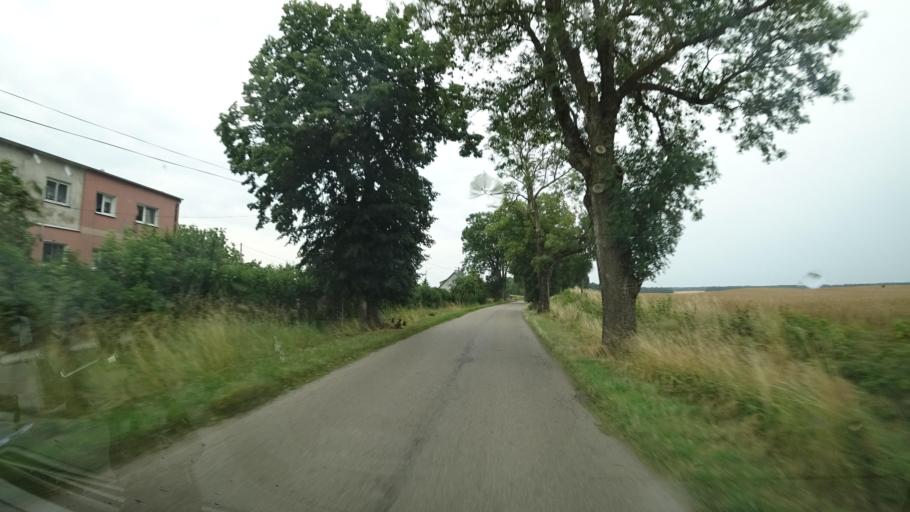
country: PL
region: Warmian-Masurian Voivodeship
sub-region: Powiat gizycki
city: Ryn
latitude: 53.9242
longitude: 21.5527
